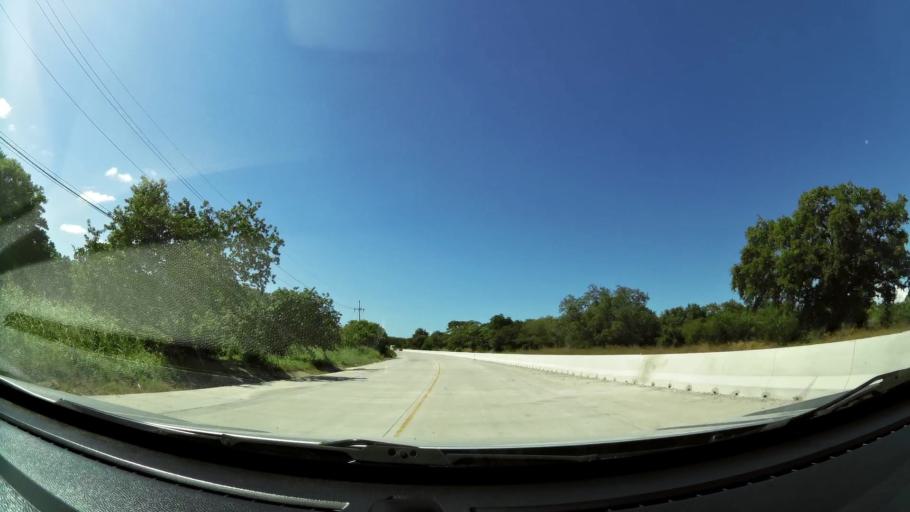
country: CR
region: Guanacaste
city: Bagaces
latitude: 10.5503
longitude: -85.3594
